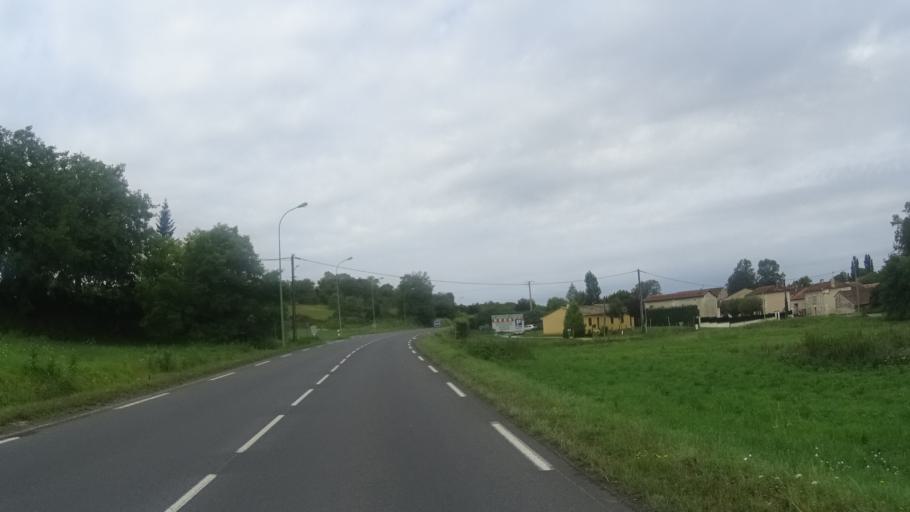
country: FR
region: Aquitaine
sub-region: Departement de la Dordogne
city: Riberac
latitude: 45.2519
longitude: 0.3630
